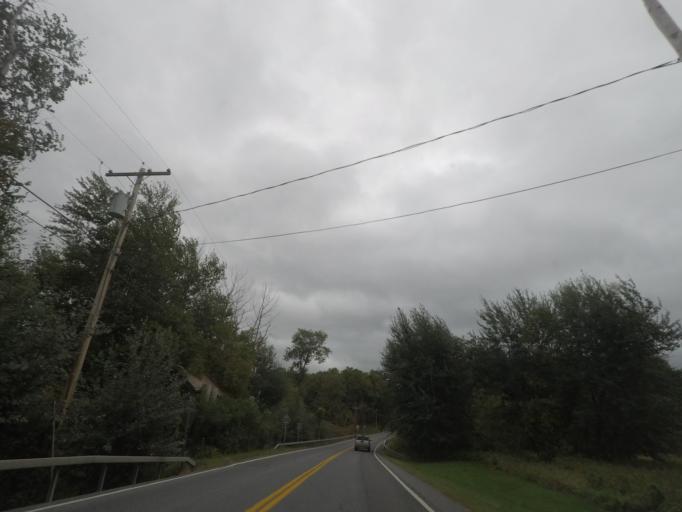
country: US
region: New York
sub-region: Washington County
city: Cambridge
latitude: 42.9537
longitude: -73.4318
